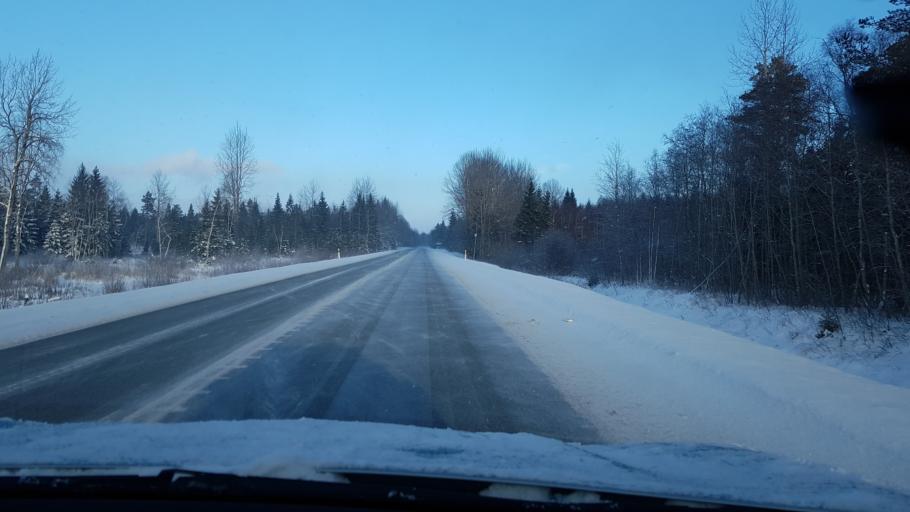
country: EE
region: Harju
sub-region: Nissi vald
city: Riisipere
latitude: 59.1622
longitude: 24.3452
